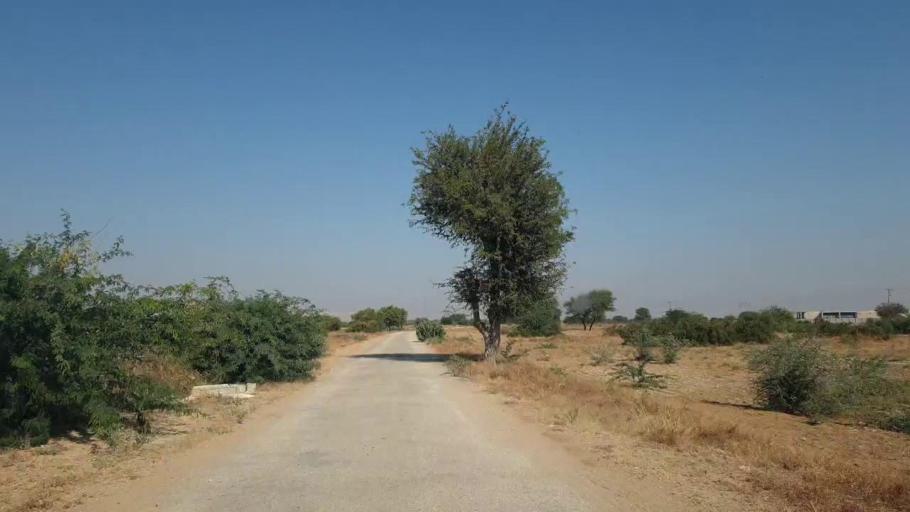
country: PK
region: Sindh
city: Gharo
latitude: 25.1800
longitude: 67.7347
